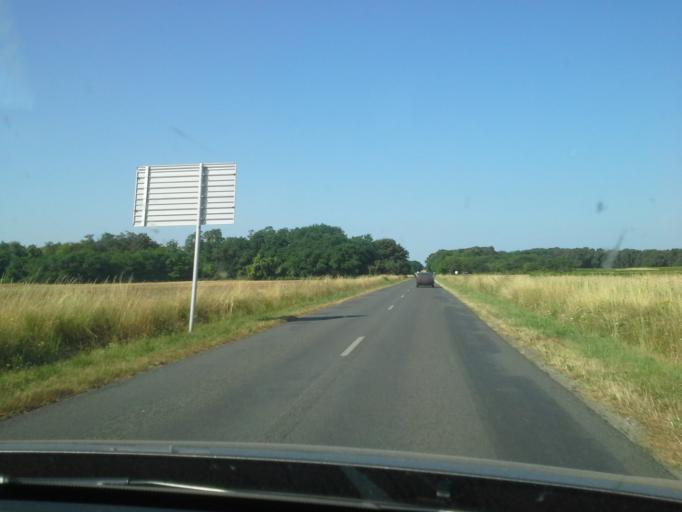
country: FR
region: Centre
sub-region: Departement du Loir-et-Cher
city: Les Montils
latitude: 47.5105
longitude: 1.2969
